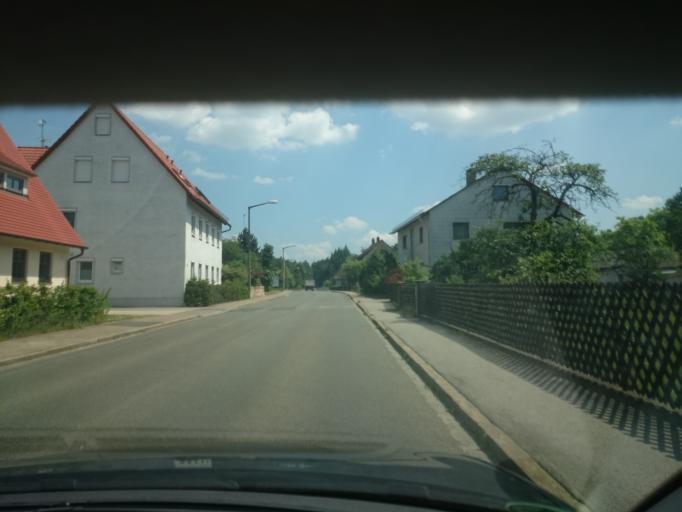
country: DE
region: Bavaria
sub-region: Regierungsbezirk Mittelfranken
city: Hilpoltstein
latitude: 49.2159
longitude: 11.1474
